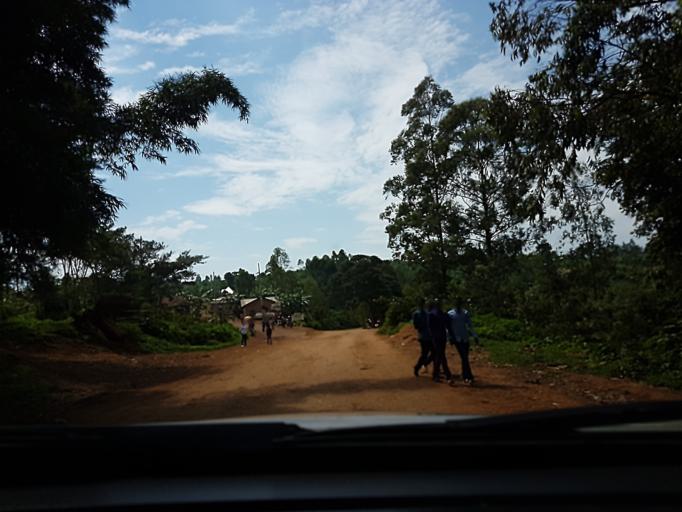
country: CD
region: South Kivu
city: Bukavu
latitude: -2.6215
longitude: 28.8770
